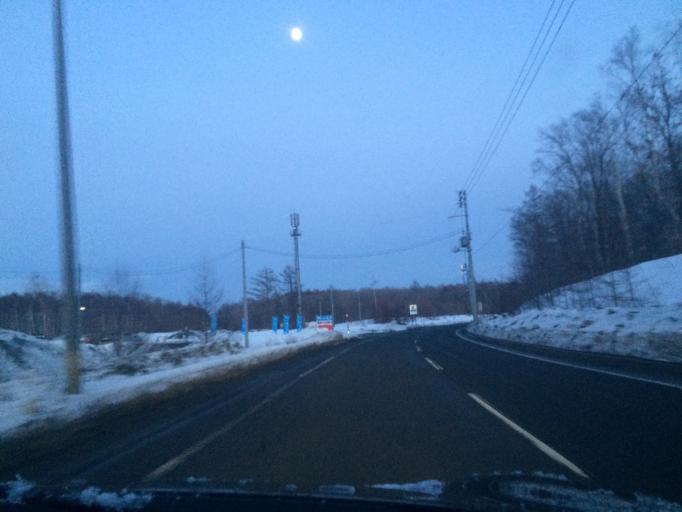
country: JP
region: Hokkaido
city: Chitose
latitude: 42.7752
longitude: 141.6559
